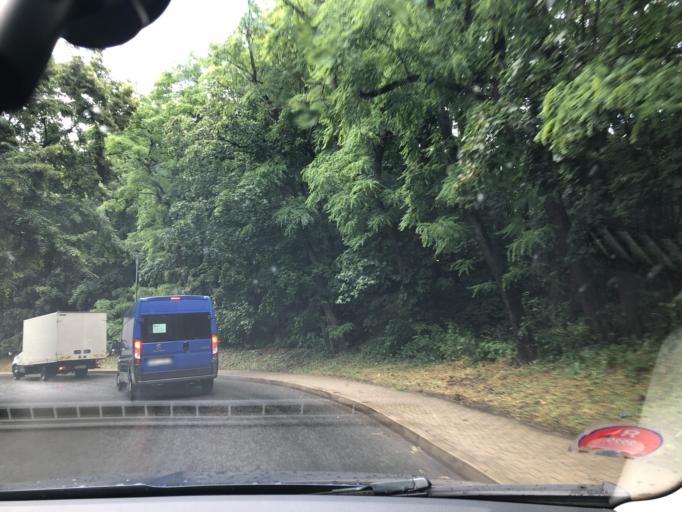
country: CZ
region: Central Bohemia
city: Kralupy nad Vltavou
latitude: 50.2347
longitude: 14.3082
